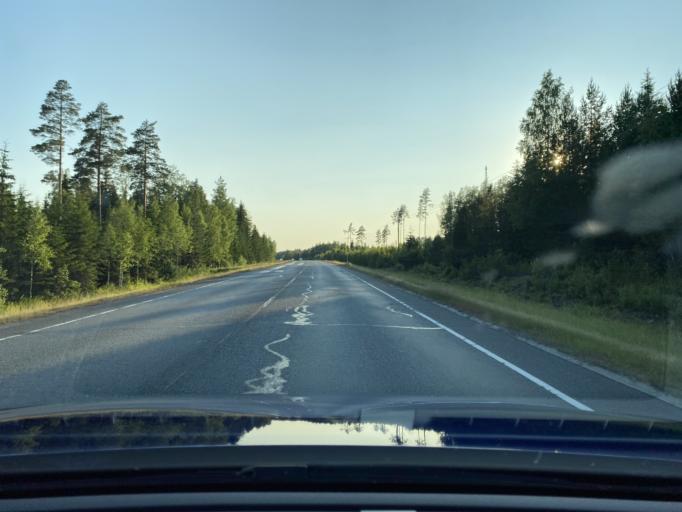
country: FI
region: Haeme
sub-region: Forssa
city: Tammela
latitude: 60.8297
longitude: 23.8754
